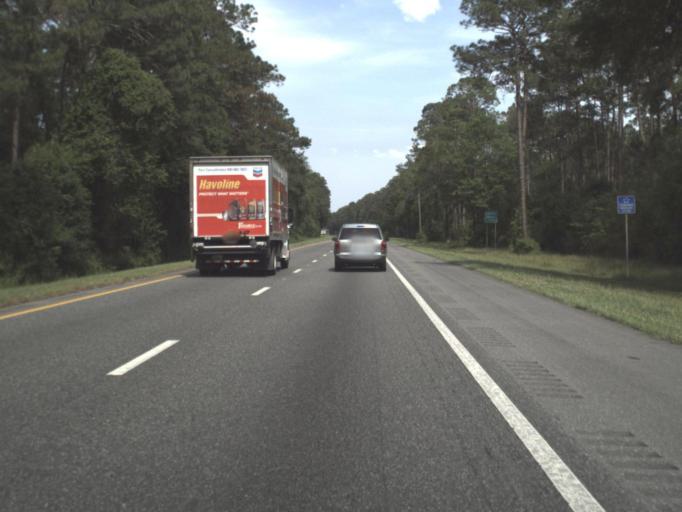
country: US
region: Florida
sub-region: Columbia County
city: Watertown
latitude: 30.2570
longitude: -82.4589
